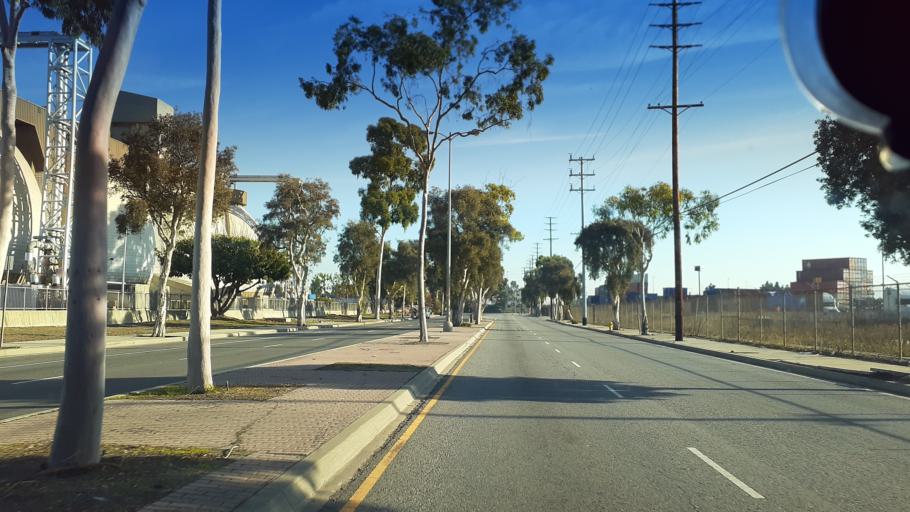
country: US
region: California
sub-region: Los Angeles County
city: San Pedro
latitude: 33.7427
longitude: -118.2631
